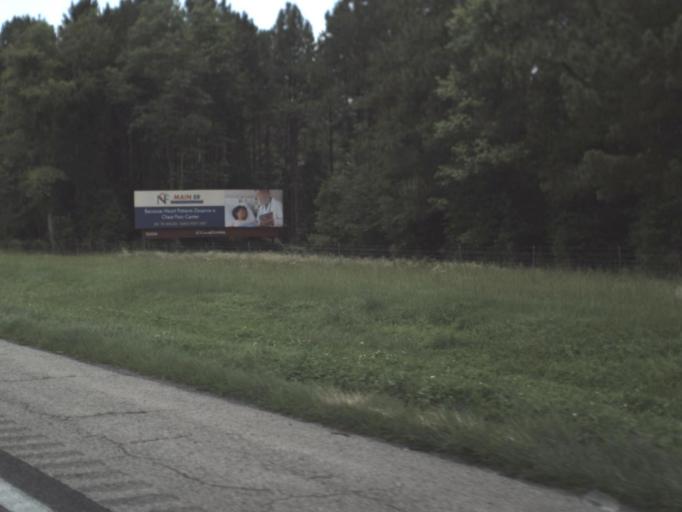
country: US
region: Florida
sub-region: Alachua County
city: Alachua
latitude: 29.7707
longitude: -82.5074
